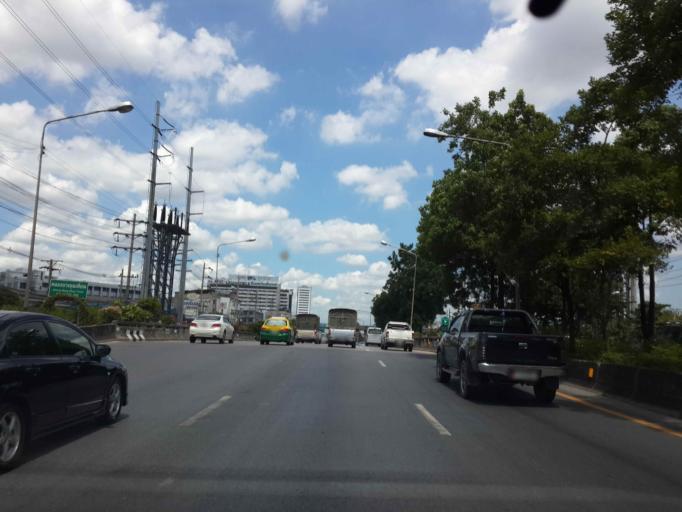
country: TH
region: Bangkok
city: Chom Thong
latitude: 13.6800
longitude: 100.4700
